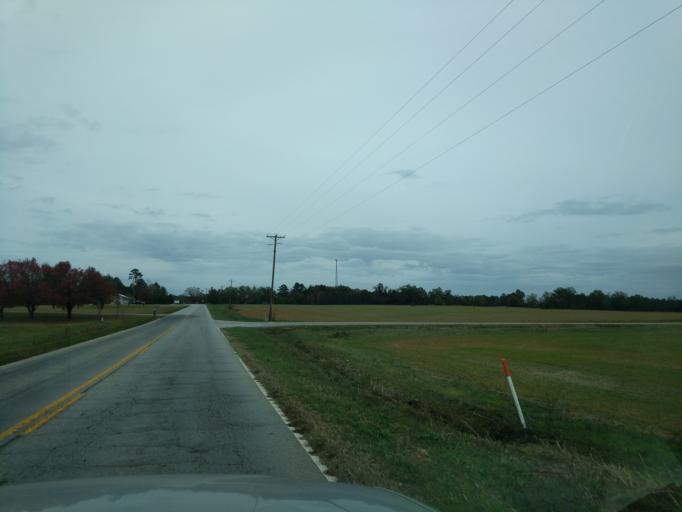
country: US
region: South Carolina
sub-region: Saluda County
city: Saluda
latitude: 34.1009
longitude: -81.7513
